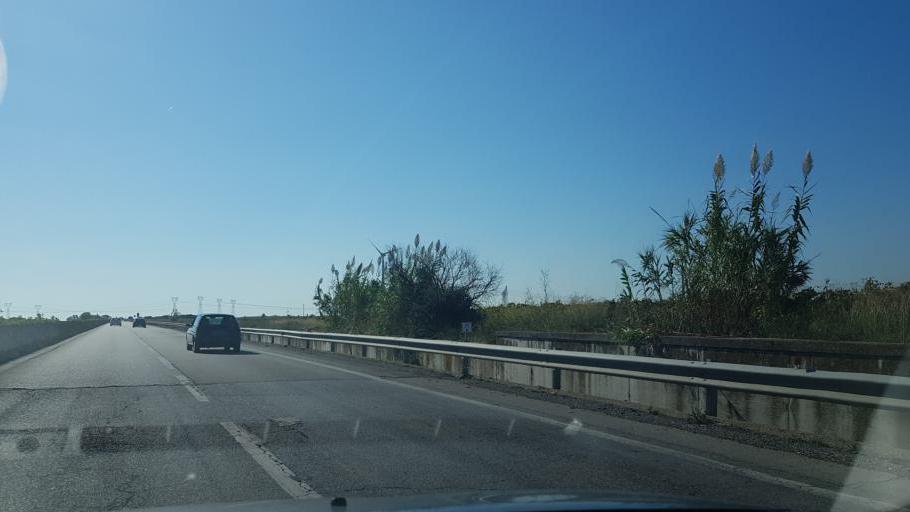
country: IT
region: Apulia
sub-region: Provincia di Brindisi
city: Tuturano
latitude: 40.5718
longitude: 17.9831
